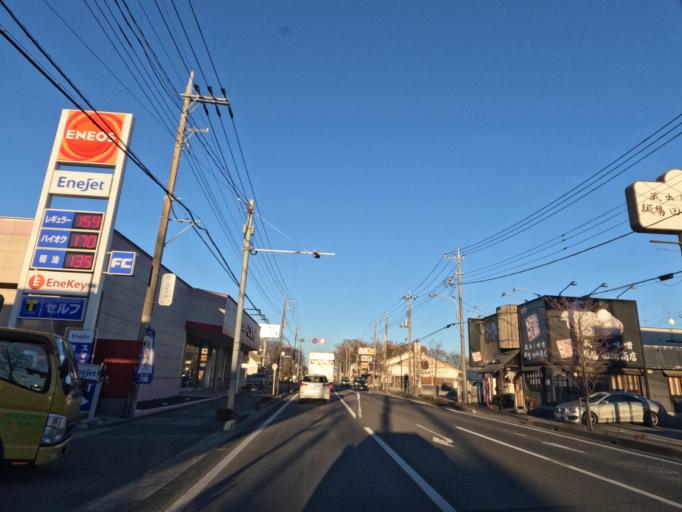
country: JP
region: Saitama
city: Iwatsuki
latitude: 35.9669
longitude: 139.6945
